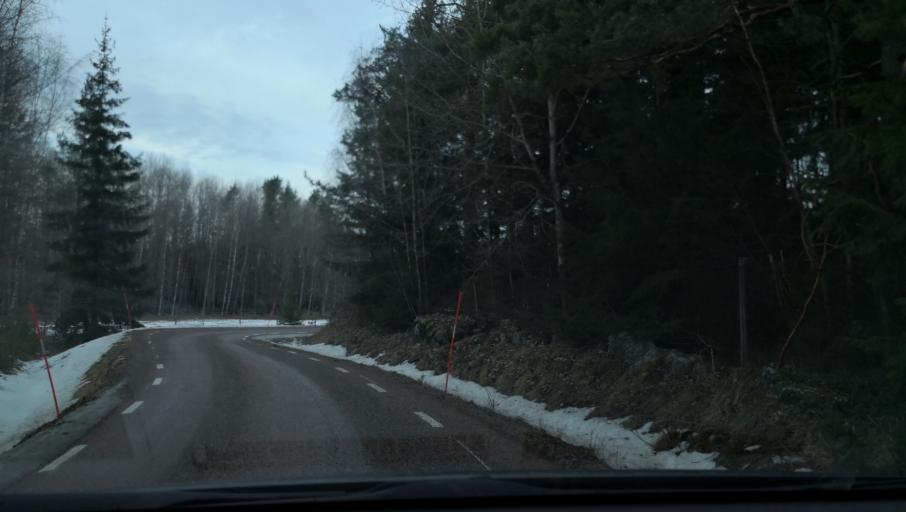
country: SE
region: Vaestmanland
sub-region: Vasteras
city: Skultuna
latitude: 59.6277
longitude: 16.4137
